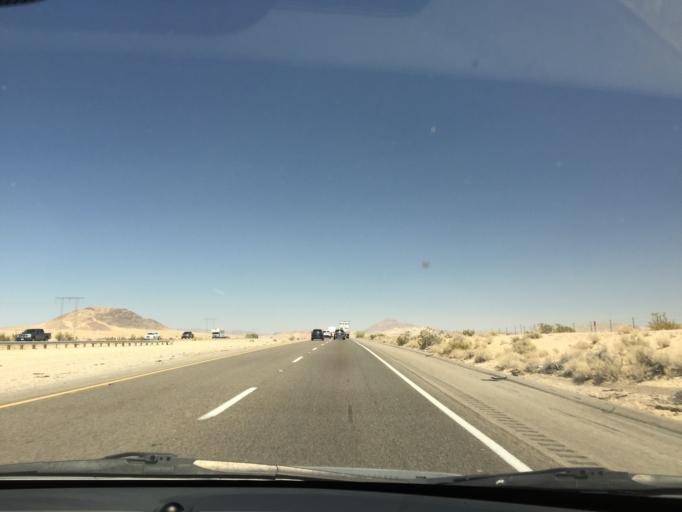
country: US
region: California
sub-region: San Bernardino County
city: Fort Irwin
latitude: 35.0174
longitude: -116.5127
